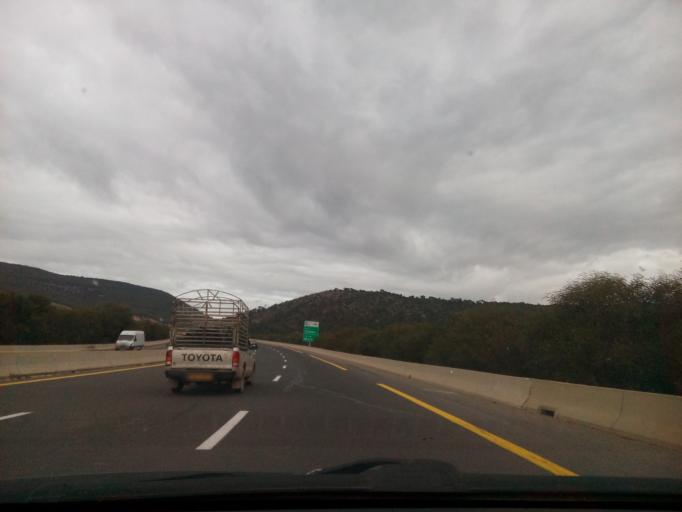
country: DZ
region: Sidi Bel Abbes
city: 'Ain el Berd
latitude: 35.3679
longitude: -0.5008
